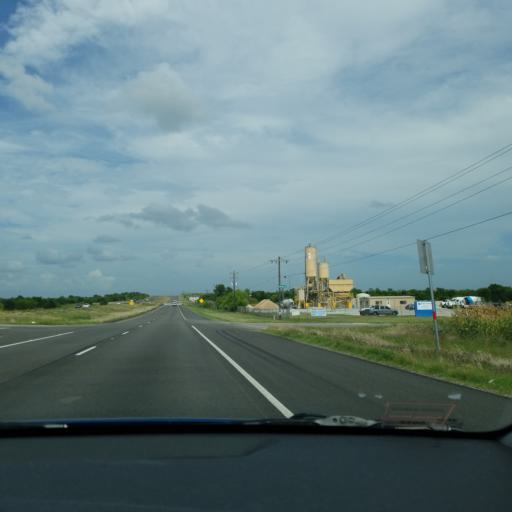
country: US
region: Texas
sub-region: Bastrop County
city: Elgin
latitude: 30.3513
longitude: -97.4629
